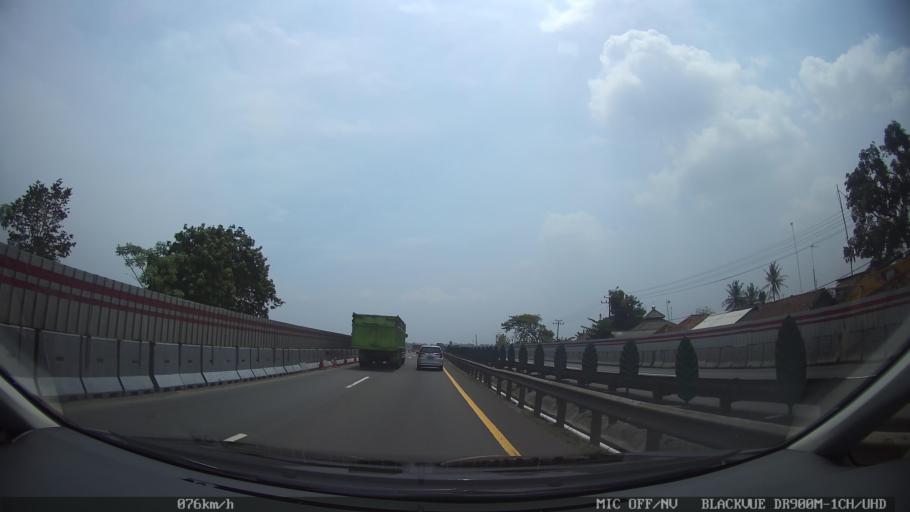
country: ID
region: West Java
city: Kresek
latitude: -6.1496
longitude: 106.3036
